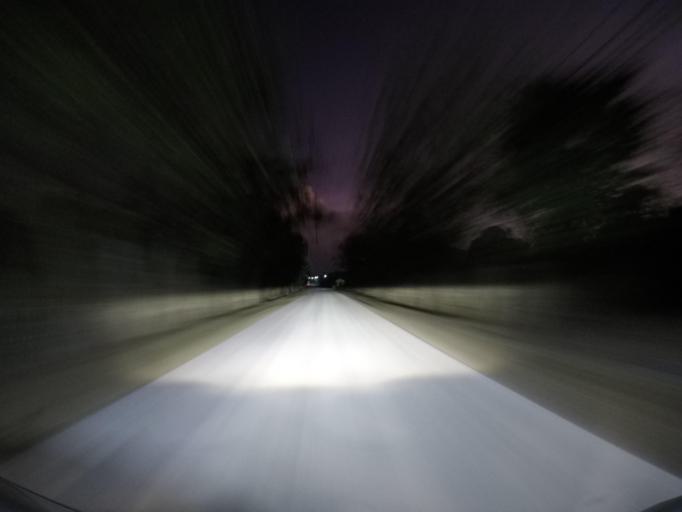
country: TL
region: Lautem
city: Lospalos
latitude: -8.4624
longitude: 126.9971
